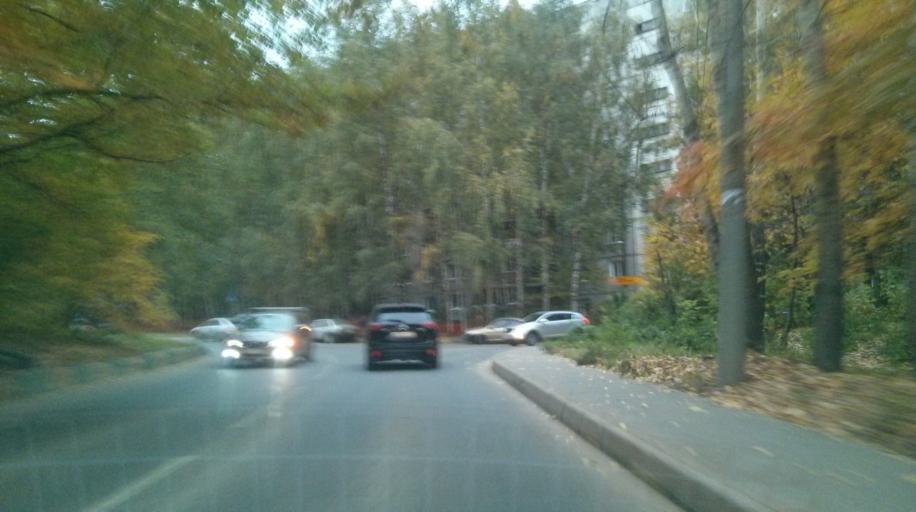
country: RU
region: Nizjnij Novgorod
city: Afonino
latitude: 56.2990
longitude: 44.0685
